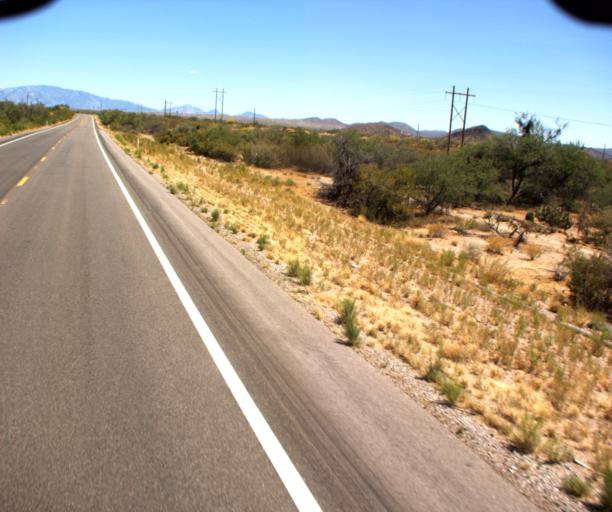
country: US
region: Arizona
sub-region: Pima County
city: Catalina
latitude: 32.6664
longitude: -111.0545
